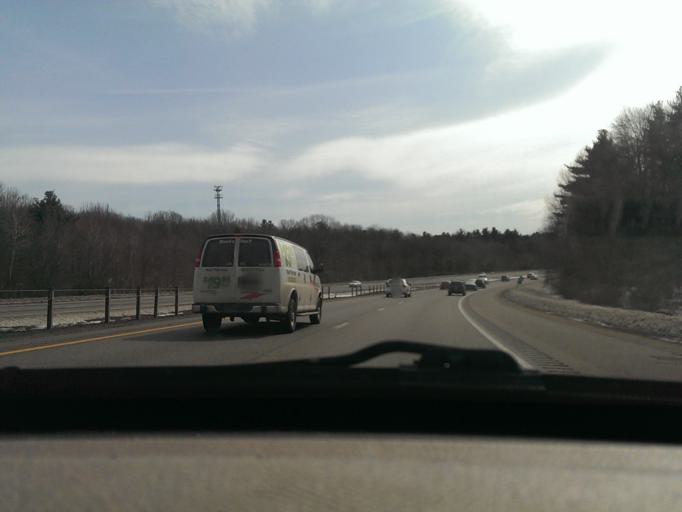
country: US
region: Massachusetts
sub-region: Worcester County
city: Whitinsville
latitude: 42.1331
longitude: -71.7021
